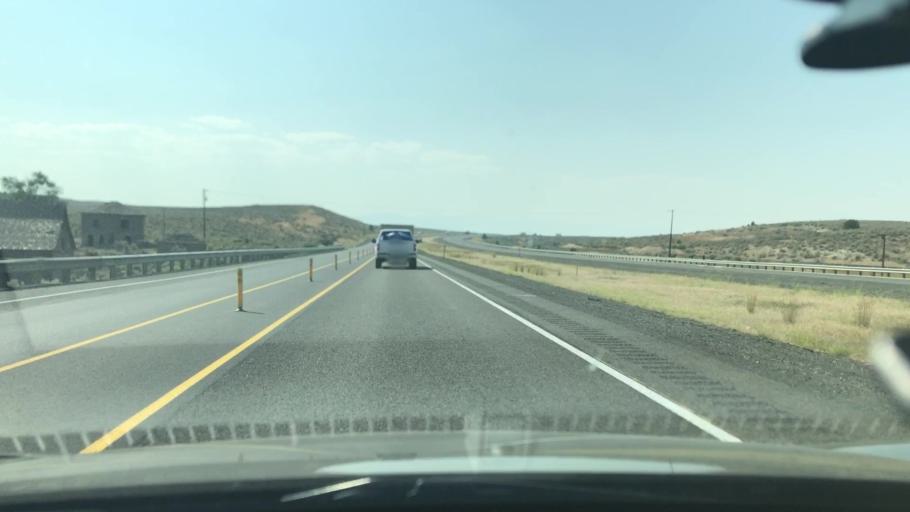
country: US
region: Oregon
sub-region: Baker County
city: Baker City
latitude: 44.6866
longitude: -117.6733
